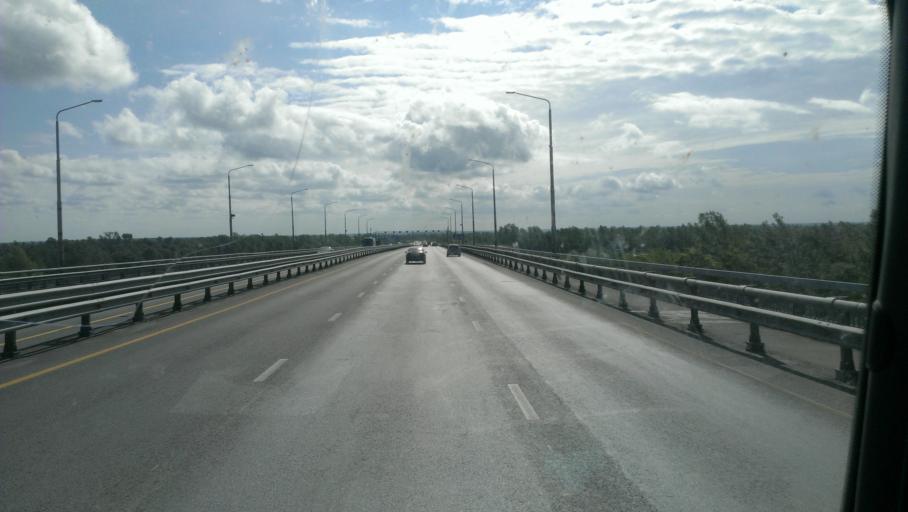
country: RU
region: Altai Krai
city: Zaton
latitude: 53.3220
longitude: 83.8075
